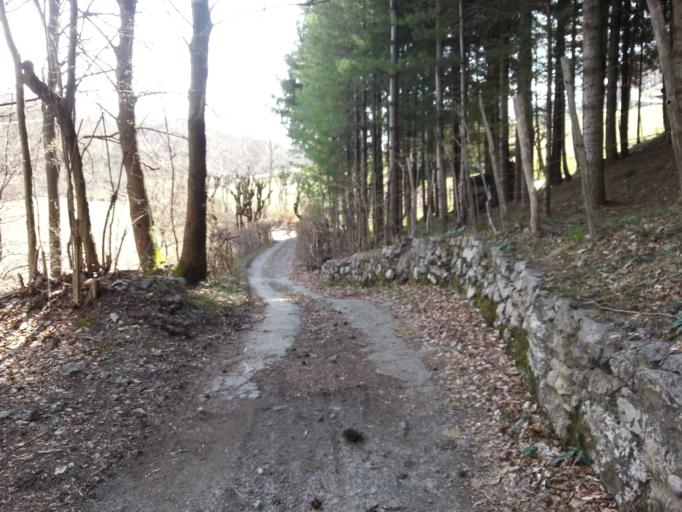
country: IT
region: Lombardy
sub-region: Provincia di Como
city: Grandola ed Uniti
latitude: 46.0065
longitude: 9.2119
